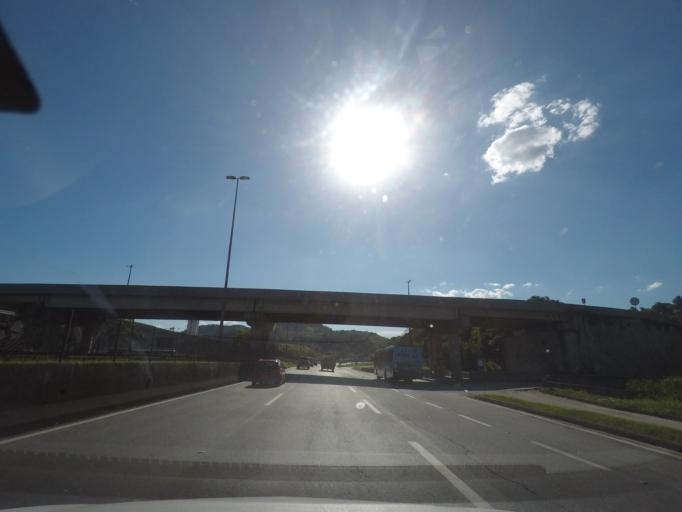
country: BR
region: Rio de Janeiro
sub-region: Petropolis
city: Petropolis
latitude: -22.6565
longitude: -43.1271
